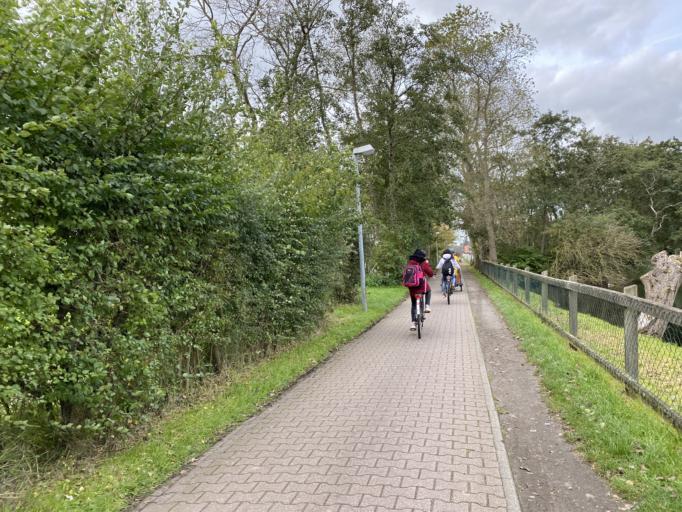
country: DE
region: Lower Saxony
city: Borkum
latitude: 53.5868
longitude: 6.6791
